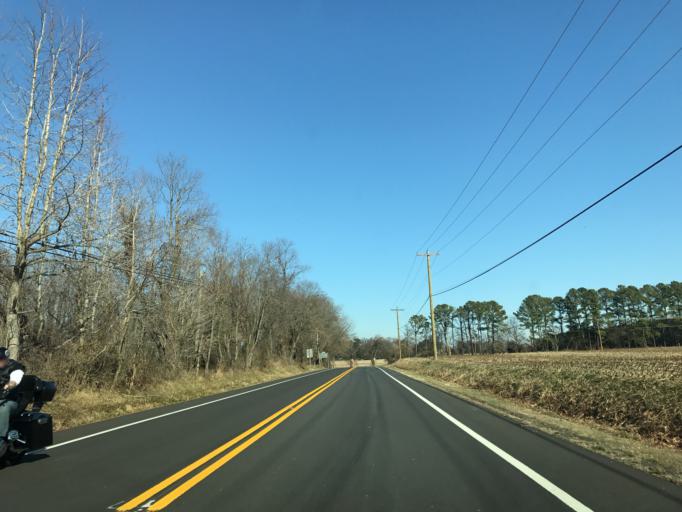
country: US
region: Maryland
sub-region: Queen Anne's County
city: Grasonville
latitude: 38.9933
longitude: -76.1451
